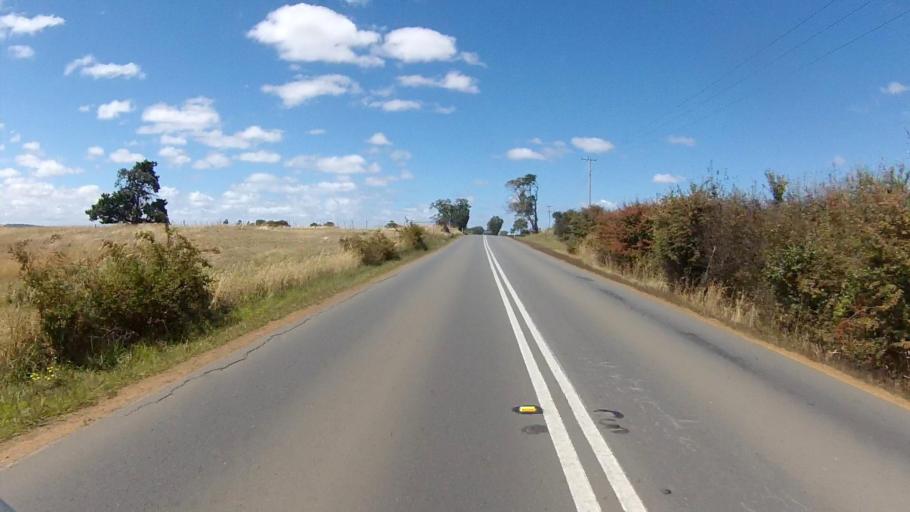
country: AU
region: Tasmania
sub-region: Clarence
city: Cambridge
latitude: -42.7739
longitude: 147.4155
